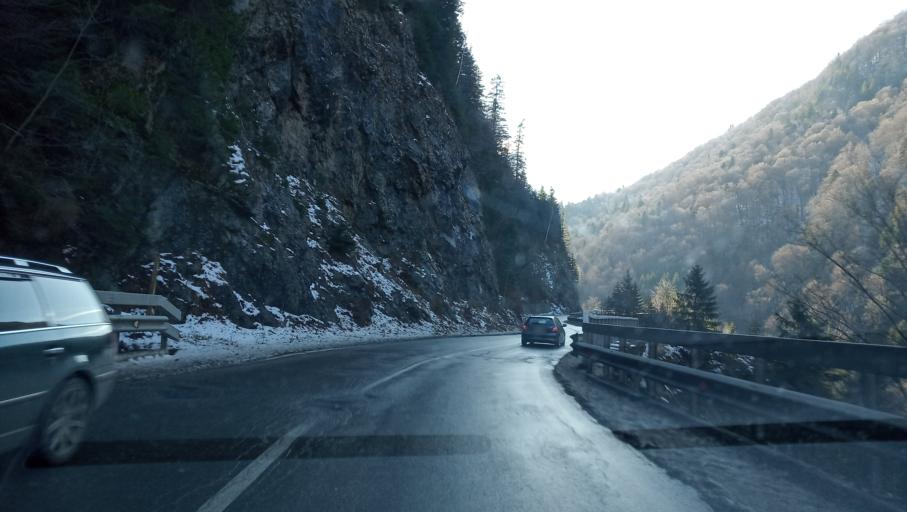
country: RO
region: Brasov
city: Crivina
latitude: 45.4740
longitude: 25.9212
